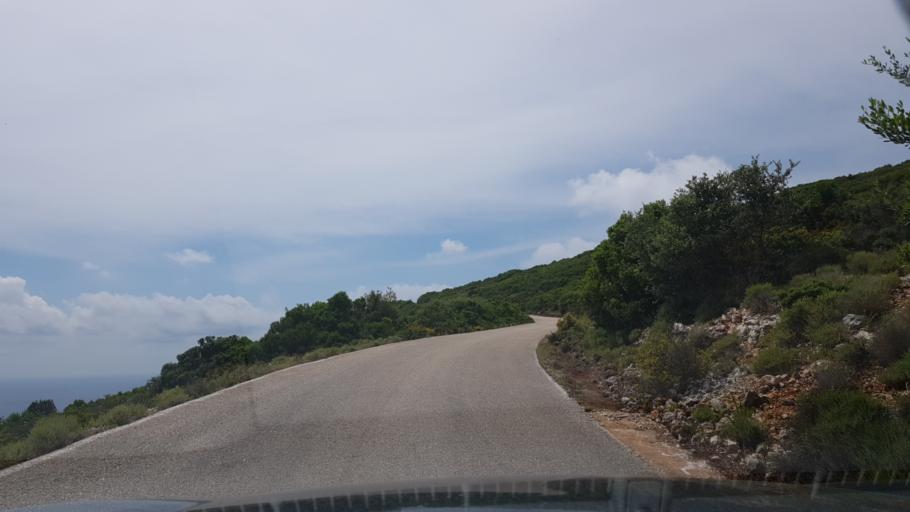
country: GR
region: Ionian Islands
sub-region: Lefkada
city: Nidri
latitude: 38.5948
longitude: 20.5562
